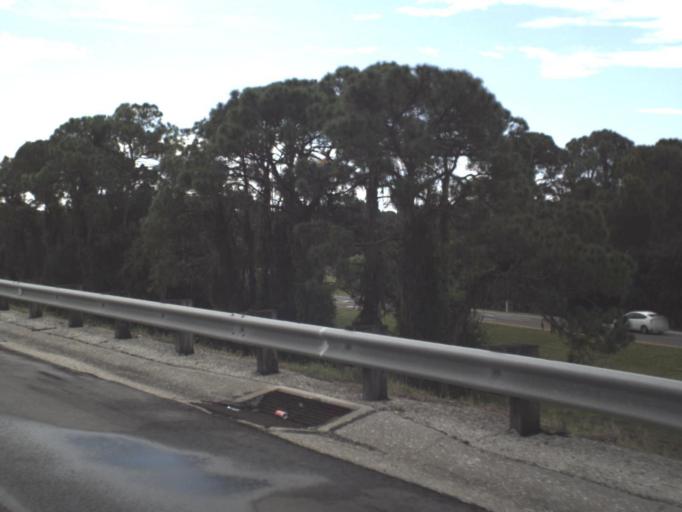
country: US
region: Florida
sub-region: Sarasota County
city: Plantation
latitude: 27.1099
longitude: -82.3497
